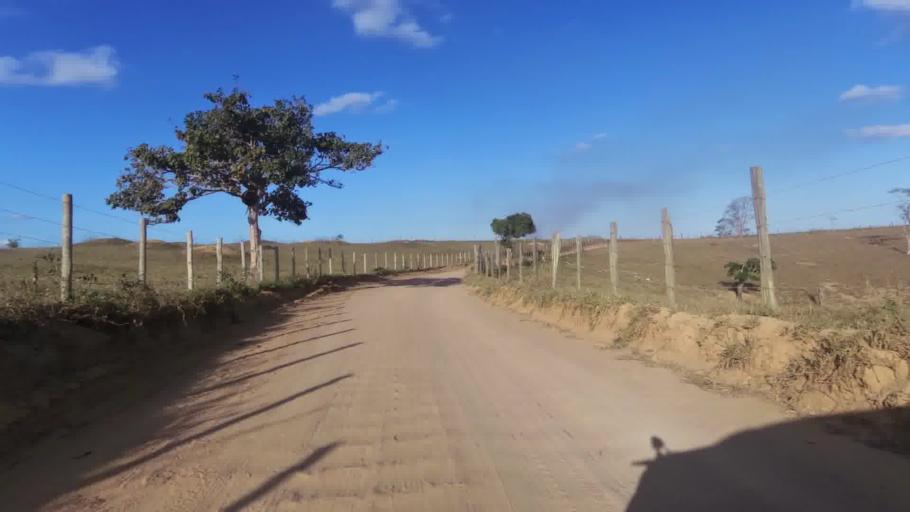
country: BR
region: Espirito Santo
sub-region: Marataizes
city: Marataizes
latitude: -21.1529
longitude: -41.0628
